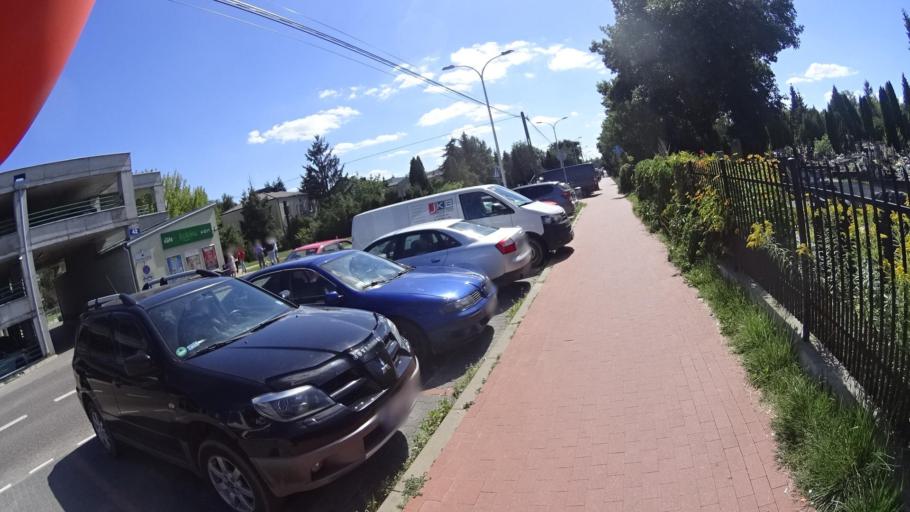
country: PL
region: Masovian Voivodeship
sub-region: Powiat piaseczynski
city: Jozefoslaw
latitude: 52.0835
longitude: 21.0430
